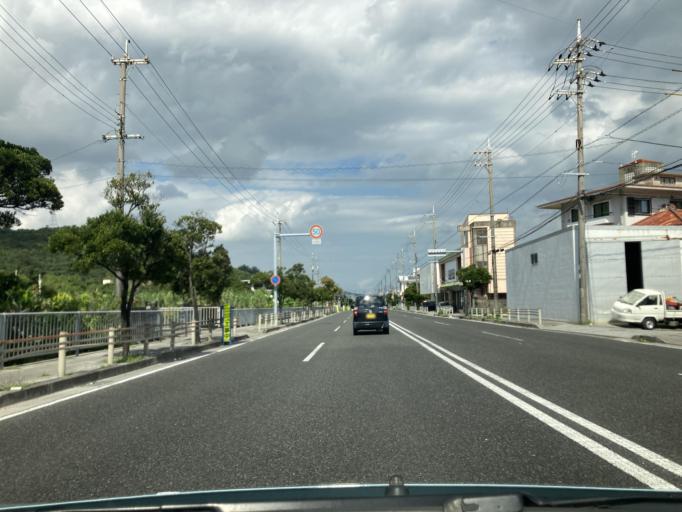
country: JP
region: Okinawa
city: Ginowan
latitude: 26.2395
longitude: 127.7772
